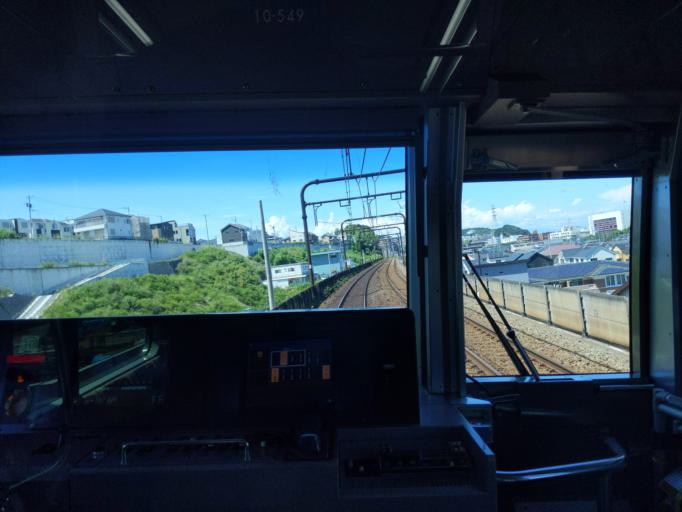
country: JP
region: Tokyo
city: Chofugaoka
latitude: 35.6337
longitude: 139.5087
